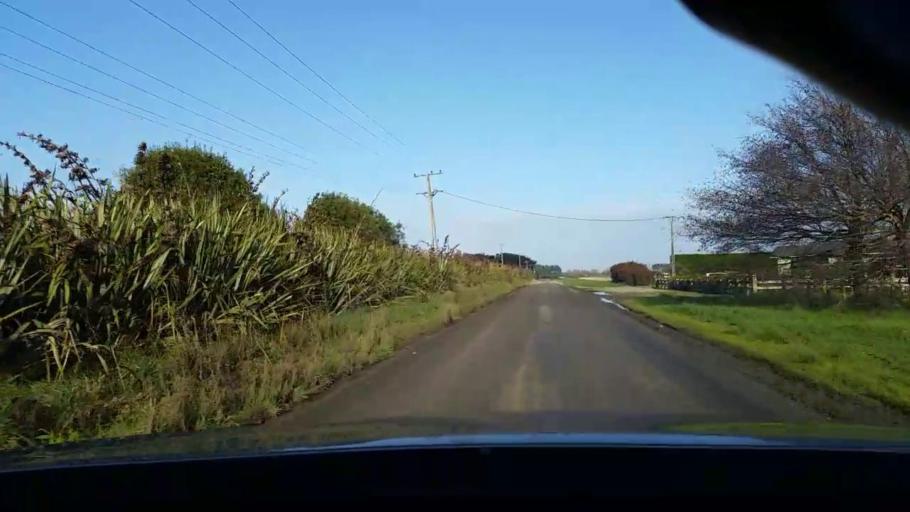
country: NZ
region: Southland
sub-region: Invercargill City
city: Invercargill
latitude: -46.3037
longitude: 168.3034
